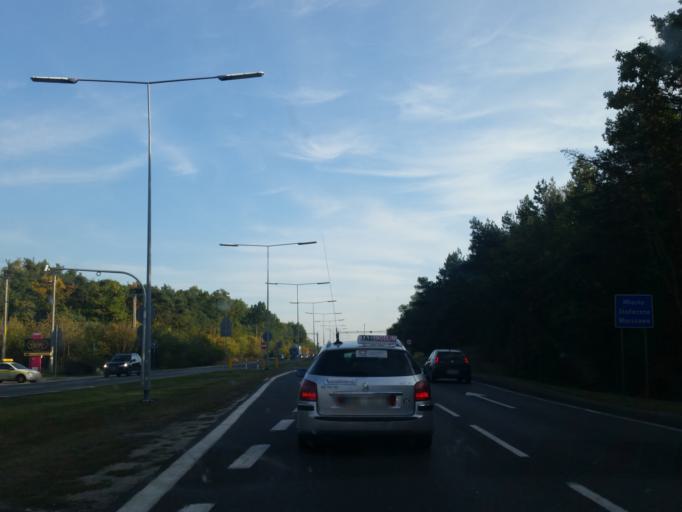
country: PL
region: Masovian Voivodeship
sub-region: Powiat warszawski zachodni
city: Lomianki
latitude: 52.3223
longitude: 20.9121
